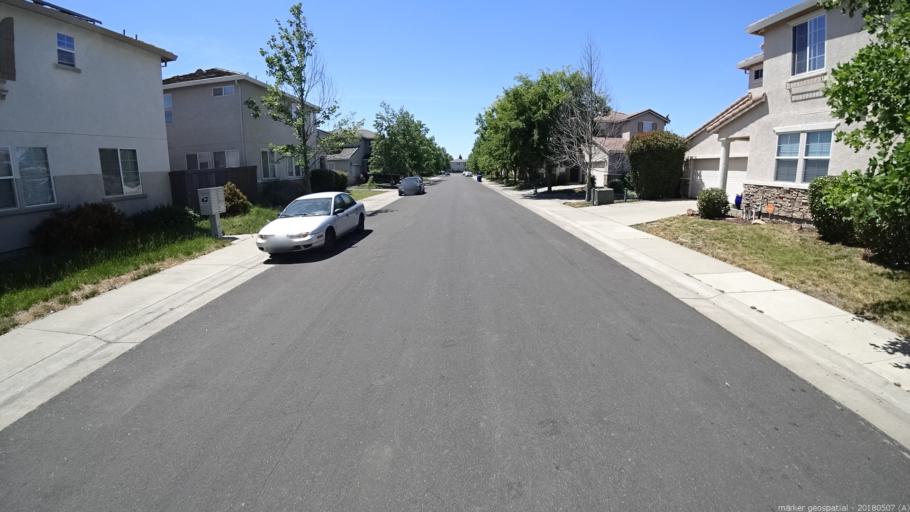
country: US
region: California
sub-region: Sacramento County
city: Elverta
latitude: 38.6738
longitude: -121.5146
